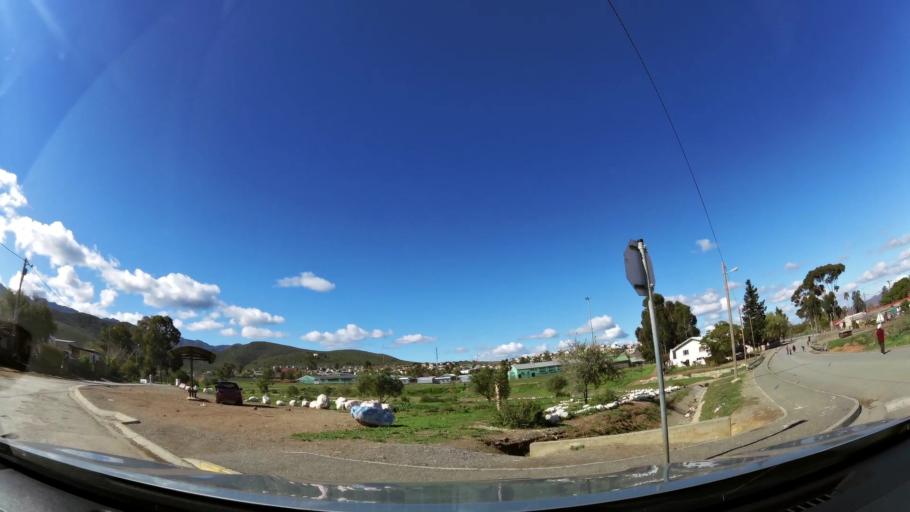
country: ZA
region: Western Cape
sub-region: Cape Winelands District Municipality
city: Ashton
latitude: -33.7867
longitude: 19.8865
